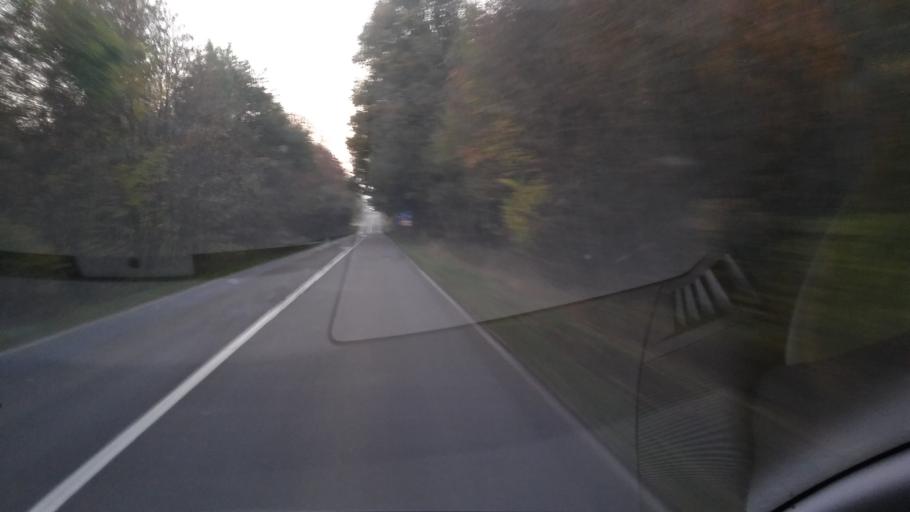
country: BE
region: Wallonia
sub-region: Province du Luxembourg
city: Etalle
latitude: 49.6605
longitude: 5.5929
